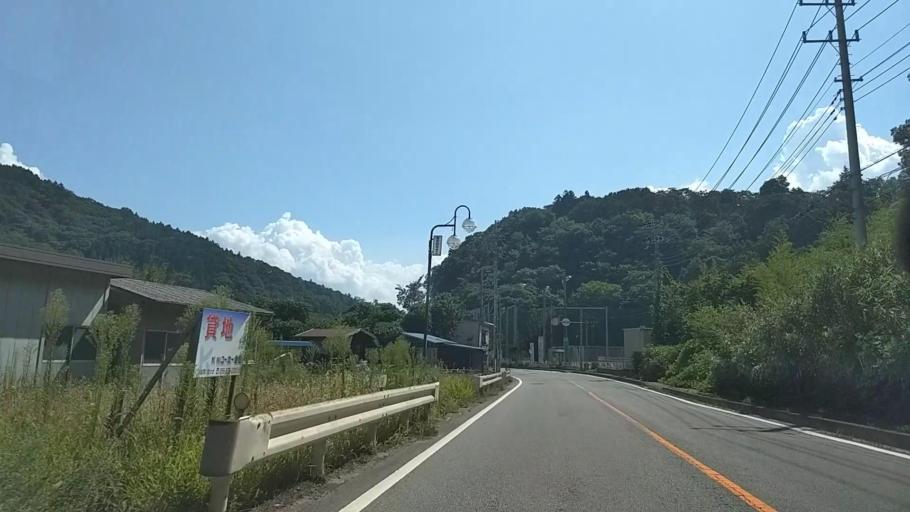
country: JP
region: Yamanashi
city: Ryuo
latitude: 35.4735
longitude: 138.4438
